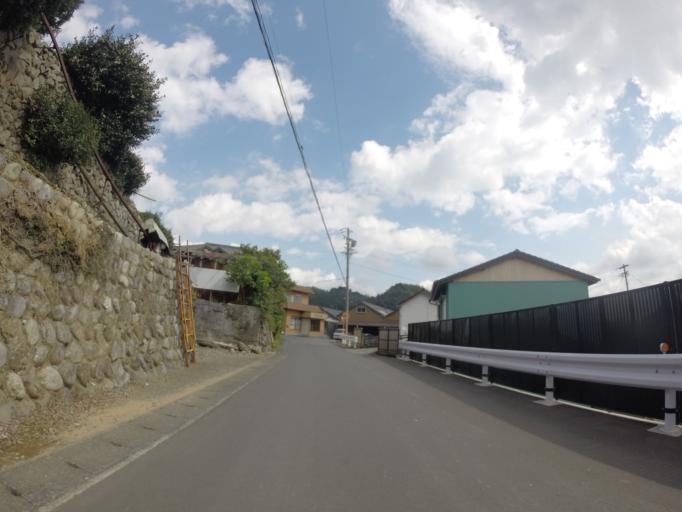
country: JP
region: Shizuoka
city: Shizuoka-shi
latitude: 35.0850
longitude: 138.4613
